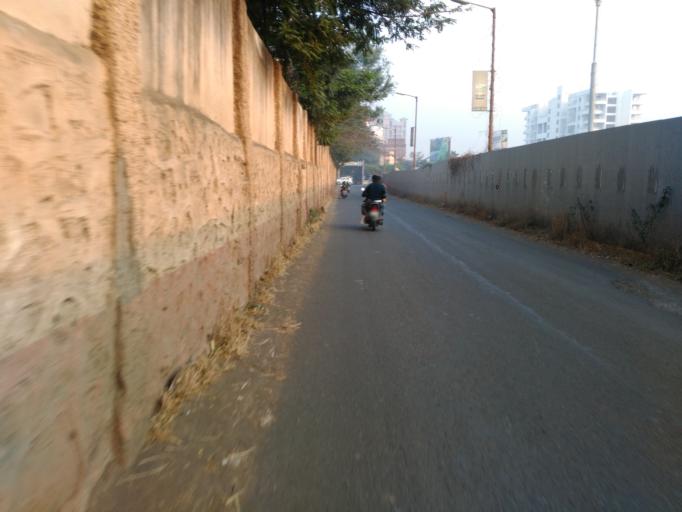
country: IN
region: Maharashtra
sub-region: Pune Division
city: Pune
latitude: 18.4519
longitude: 73.8839
